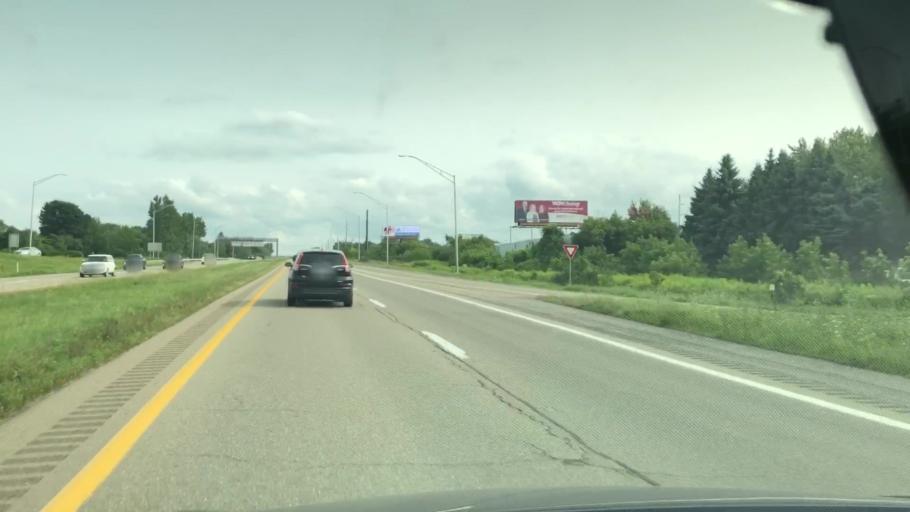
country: US
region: Pennsylvania
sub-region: Erie County
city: Erie
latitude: 42.0924
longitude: -80.1208
